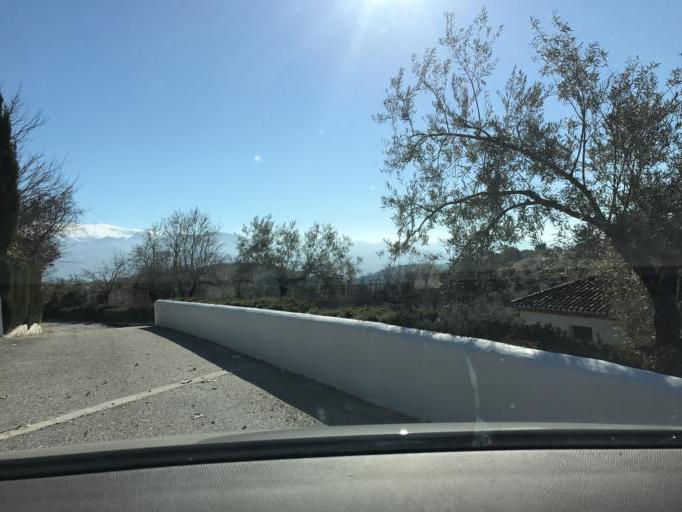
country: ES
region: Andalusia
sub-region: Provincia de Granada
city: Huetor Santillan
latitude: 37.2123
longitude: -3.5332
